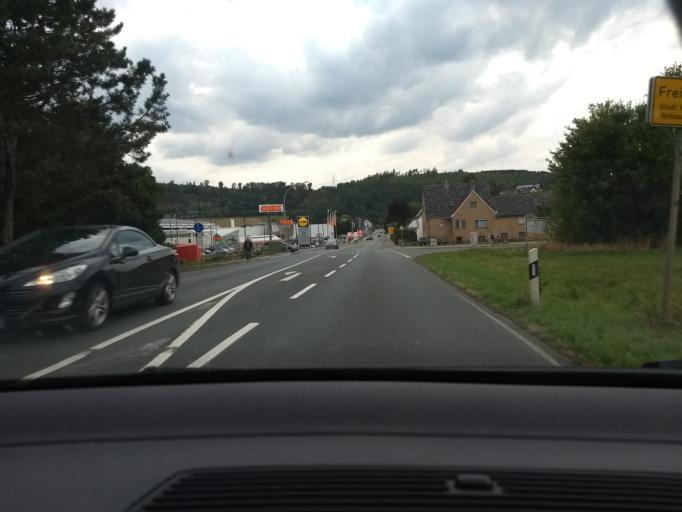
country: DE
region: North Rhine-Westphalia
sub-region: Regierungsbezirk Arnsberg
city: Arnsberg
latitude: 51.3637
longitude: 8.1771
